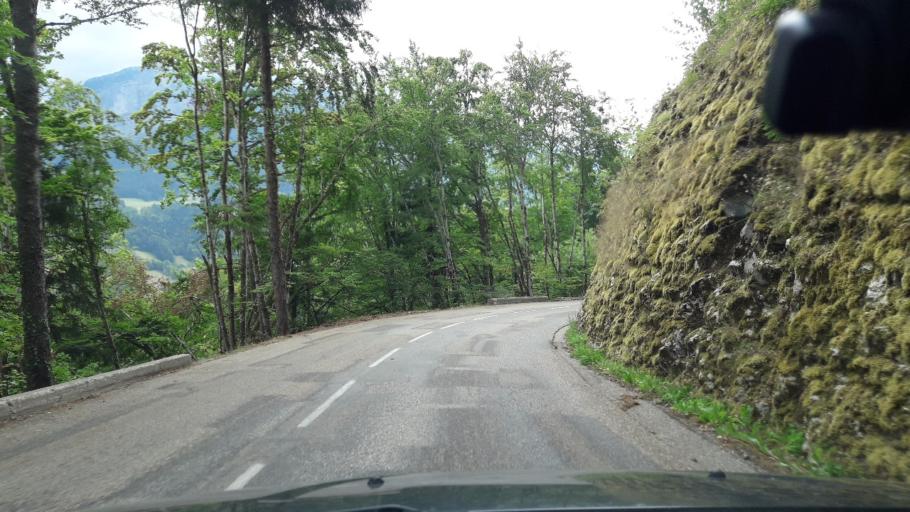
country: FR
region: Rhone-Alpes
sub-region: Departement de la Savoie
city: Vimines
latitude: 45.4526
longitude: 5.8699
